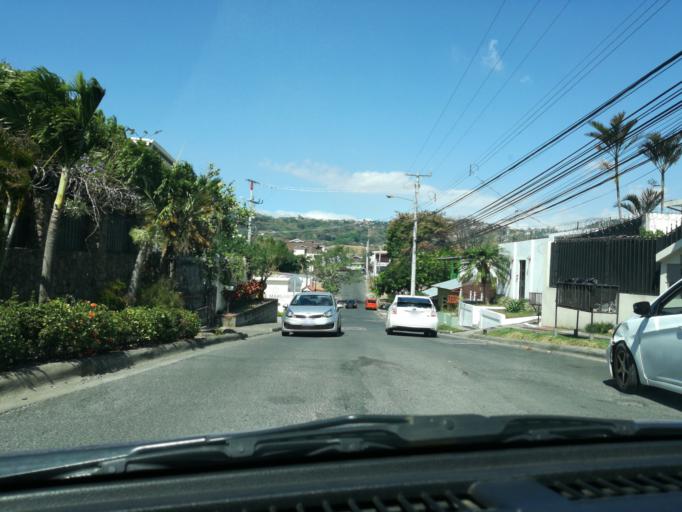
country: CR
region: San Jose
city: Santa Ana
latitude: 9.9404
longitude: -84.1872
